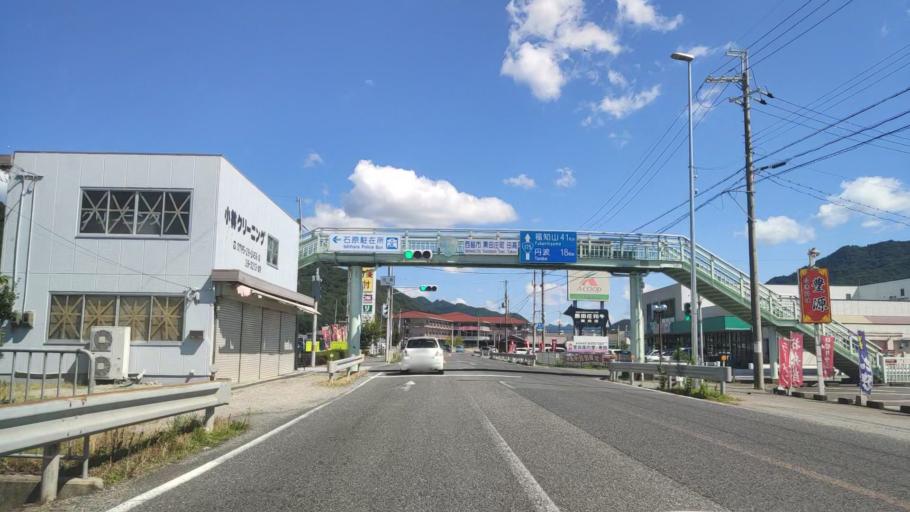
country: JP
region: Hyogo
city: Nishiwaki
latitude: 35.0559
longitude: 134.9918
